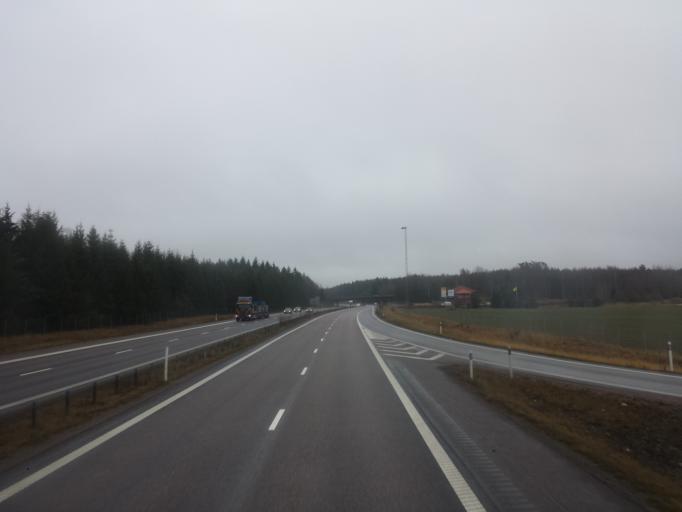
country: SE
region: Soedermanland
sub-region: Nykopings Kommun
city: Svalsta
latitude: 58.7479
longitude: 16.9247
